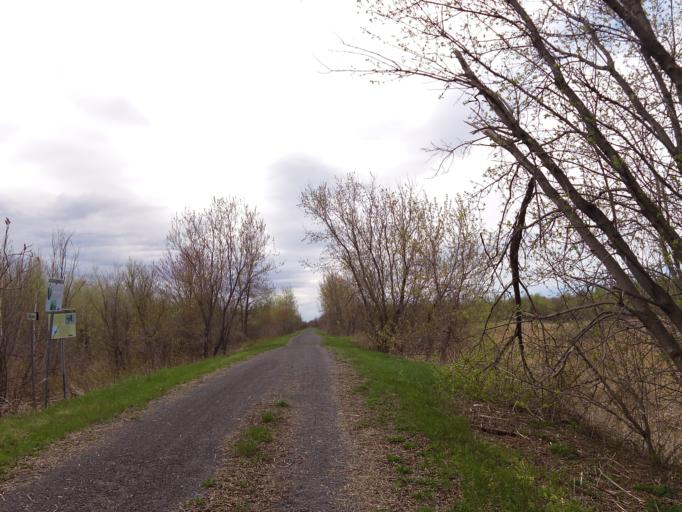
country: CA
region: Ontario
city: Hawkesbury
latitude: 45.5437
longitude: -74.7669
